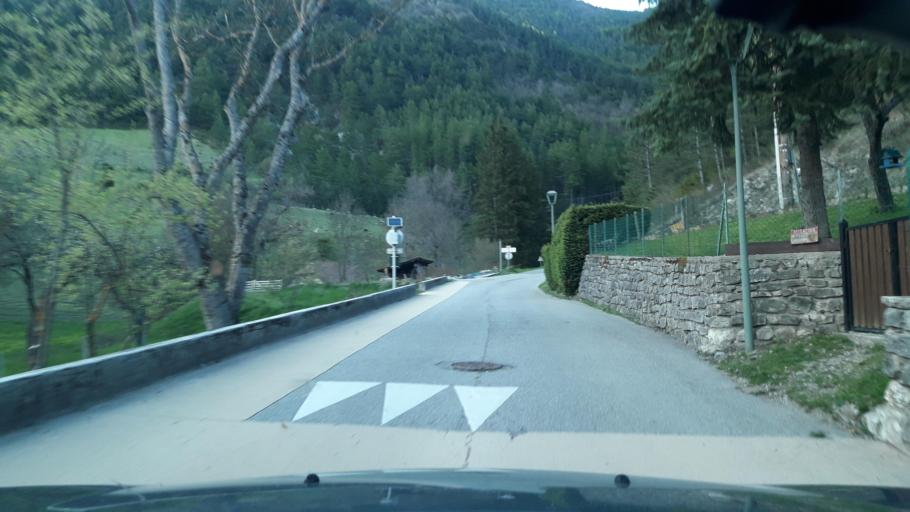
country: FR
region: Rhone-Alpes
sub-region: Departement de l'Isere
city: Mens
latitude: 44.6894
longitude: 5.5970
